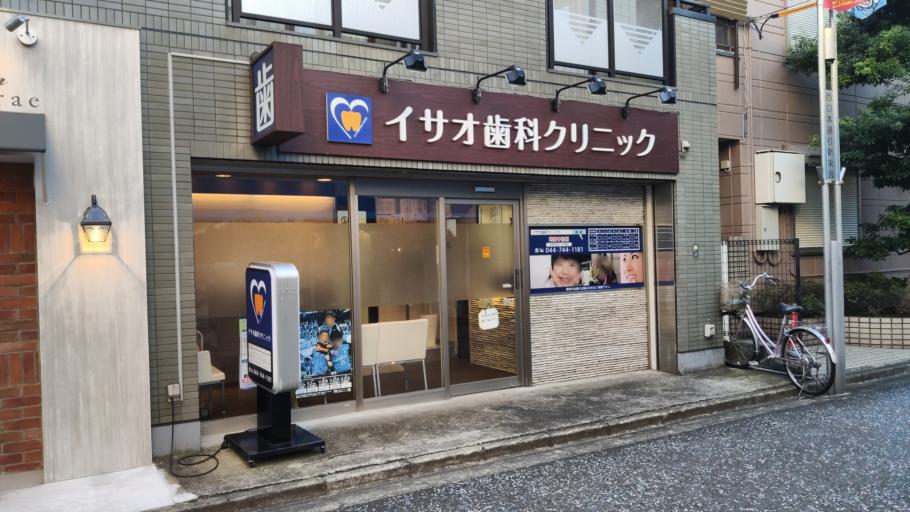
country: JP
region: Kanagawa
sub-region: Kawasaki-shi
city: Kawasaki
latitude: 35.5805
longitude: 139.6595
